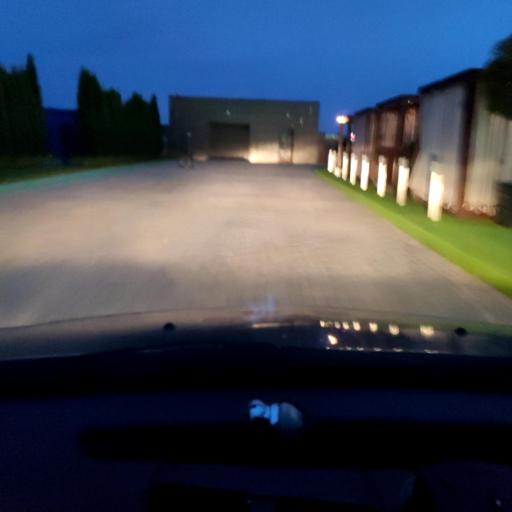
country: RU
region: Voronezj
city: Podgornoye
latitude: 51.7842
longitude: 39.1994
